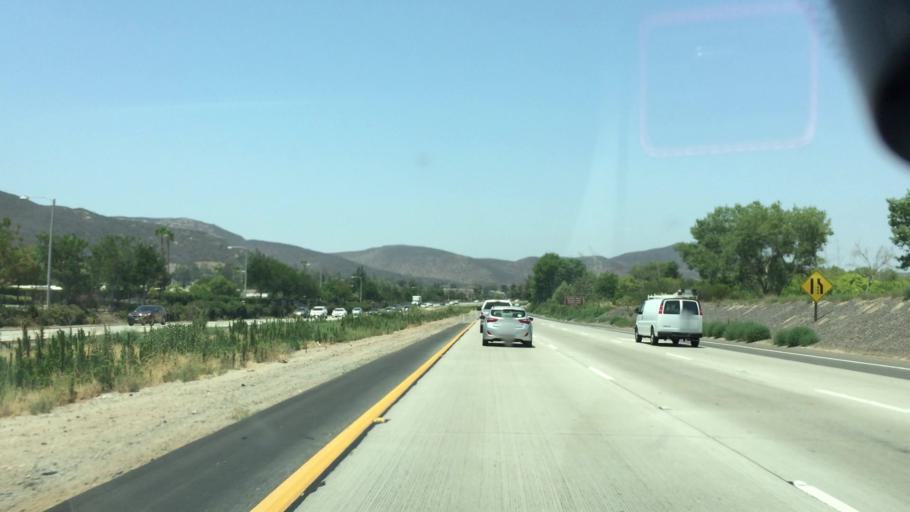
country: US
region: California
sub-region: San Diego County
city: Santee
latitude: 32.8361
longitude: -117.0141
